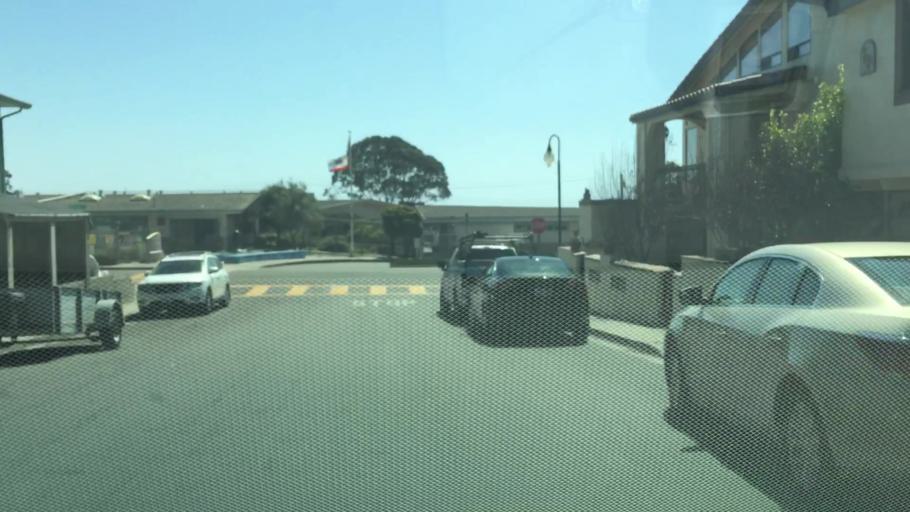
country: US
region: California
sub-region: San Mateo County
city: El Granada
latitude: 37.5004
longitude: -122.4646
